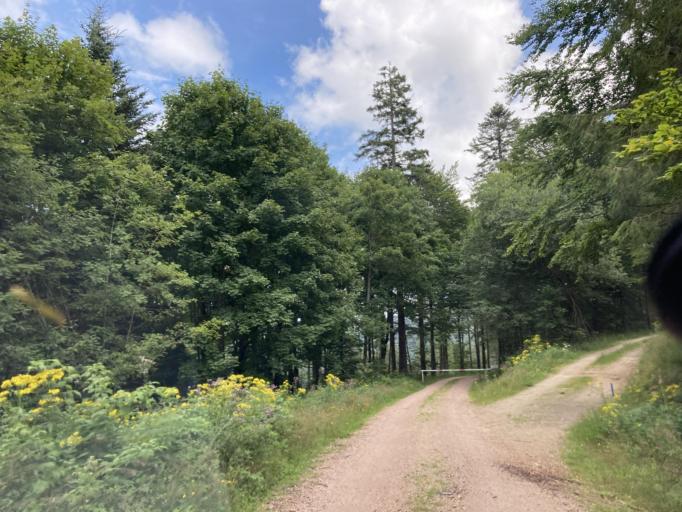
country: DE
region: Baden-Wuerttemberg
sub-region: Freiburg Region
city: Schonach im Schwarzwald
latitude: 48.1435
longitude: 8.1464
